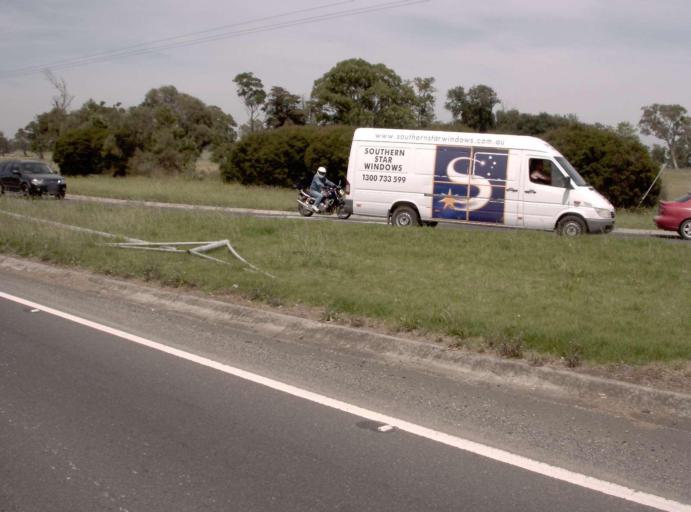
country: AU
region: Victoria
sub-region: Casey
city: Lynbrook
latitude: -38.0779
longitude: 145.2395
